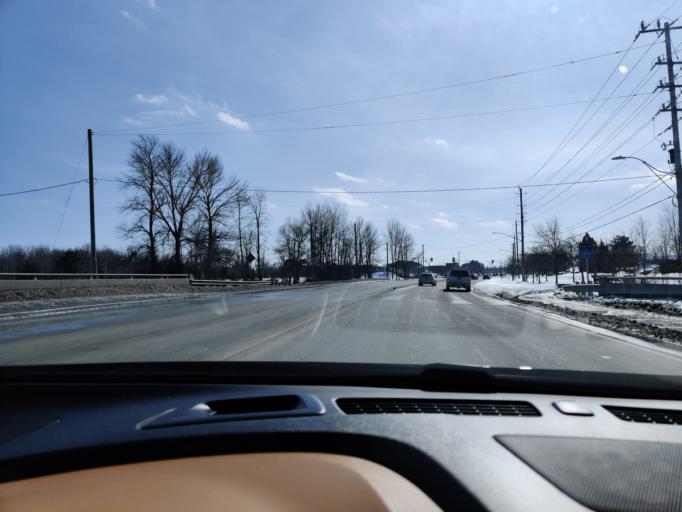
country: CA
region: Ontario
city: Collingwood
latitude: 44.5063
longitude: -80.2358
